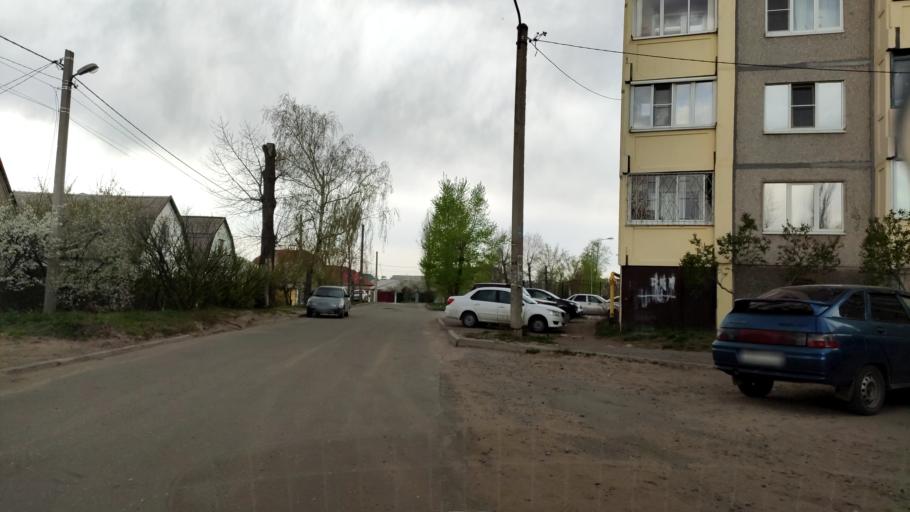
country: RU
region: Voronezj
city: Pridonskoy
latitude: 51.6818
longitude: 39.0794
